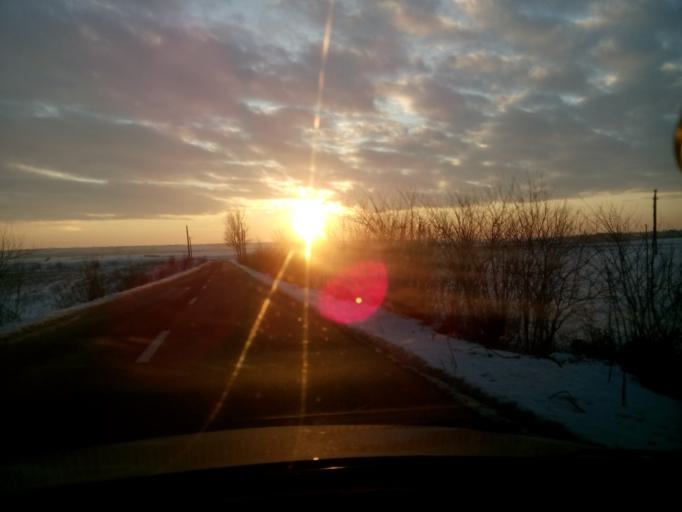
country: RO
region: Calarasi
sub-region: Comuna Soldanu
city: Soldanu
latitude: 44.2195
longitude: 26.5421
